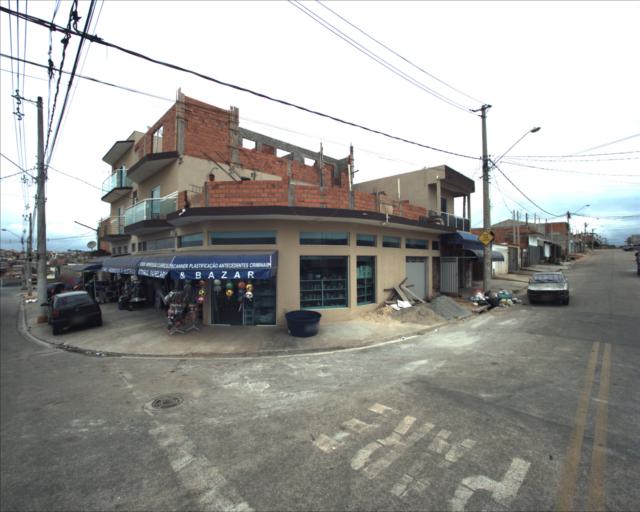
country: BR
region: Sao Paulo
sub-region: Sorocaba
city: Sorocaba
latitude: -23.4322
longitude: -47.5029
